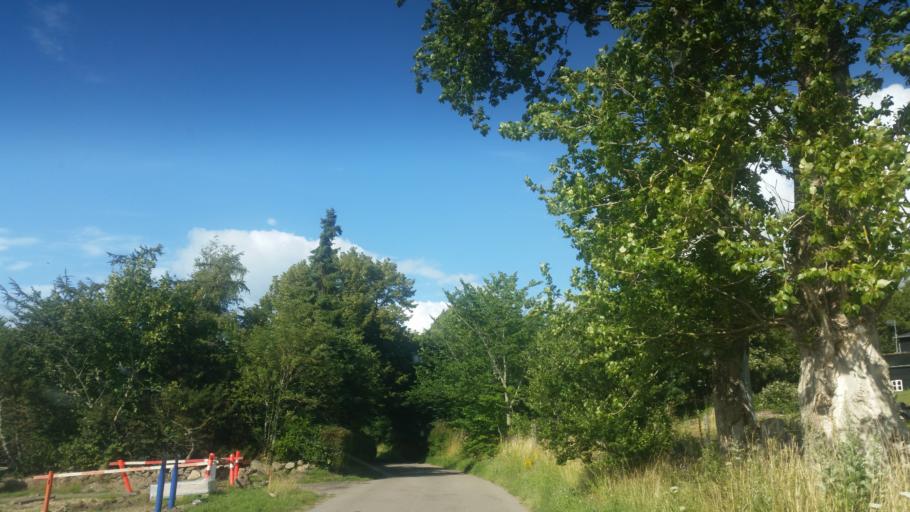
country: DK
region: Zealand
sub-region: Odsherred Kommune
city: Horve
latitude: 55.8159
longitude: 11.4054
